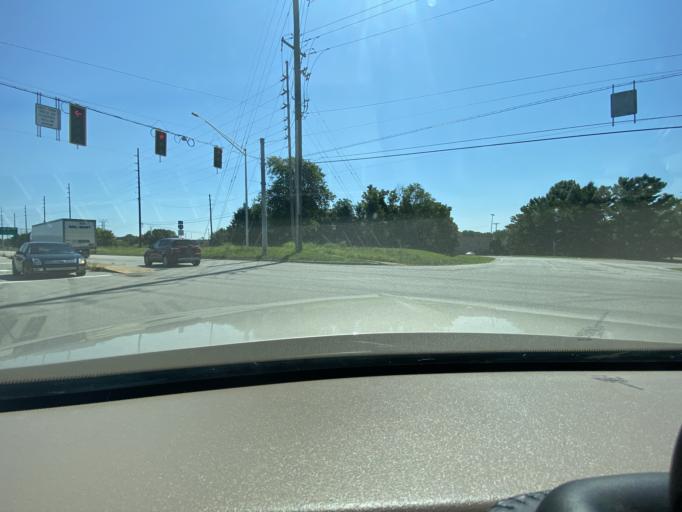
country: US
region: Indiana
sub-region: Monroe County
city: Bloomington
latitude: 39.1451
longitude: -86.5778
